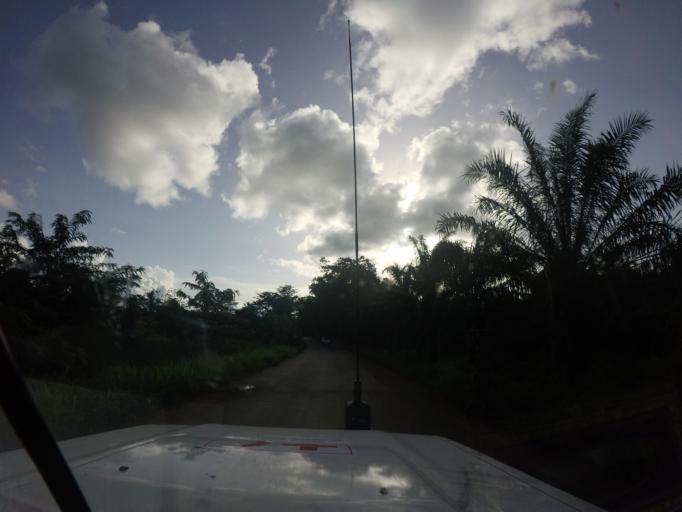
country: GN
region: Kindia
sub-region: Kindia
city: Kindia
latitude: 10.0035
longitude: -12.7675
